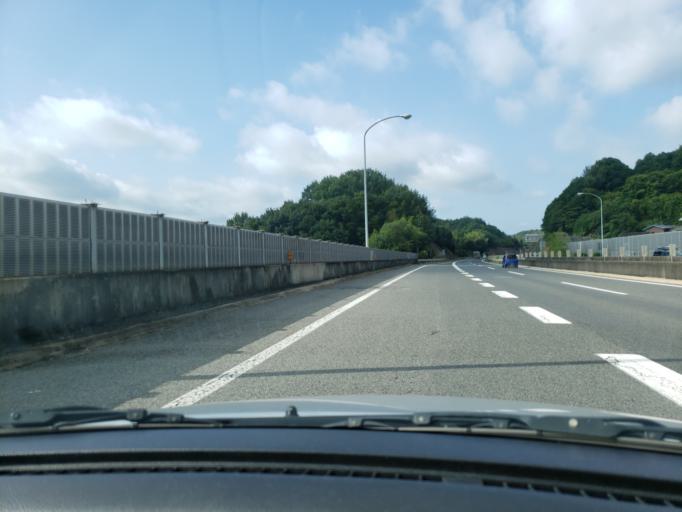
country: JP
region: Hiroshima
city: Fukuyama
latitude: 34.4879
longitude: 133.3140
